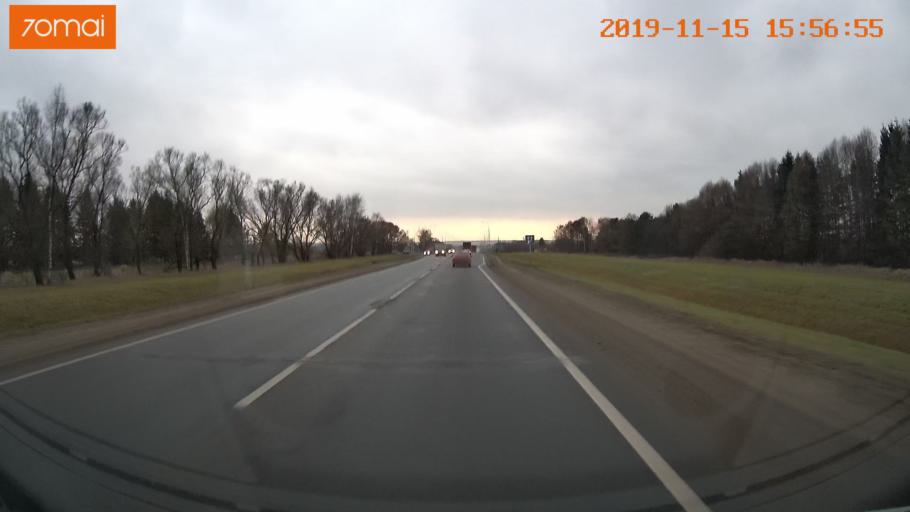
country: RU
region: Jaroslavl
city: Yaroslavl
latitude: 57.8365
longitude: 39.9687
